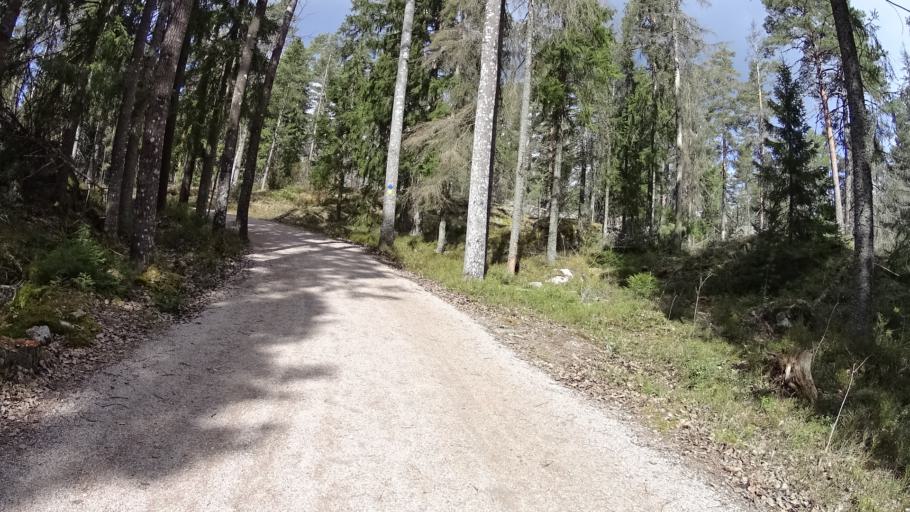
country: FI
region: Uusimaa
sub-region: Helsinki
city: Espoo
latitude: 60.2723
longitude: 24.6304
